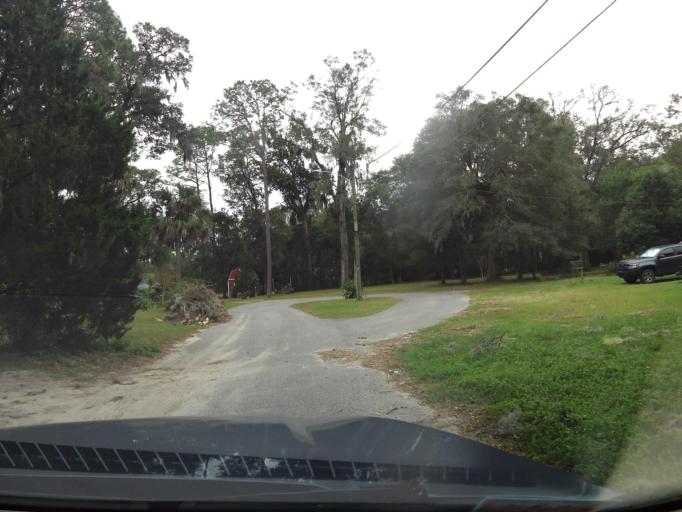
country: US
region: Florida
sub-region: Duval County
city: Jacksonville
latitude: 30.3079
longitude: -81.6016
